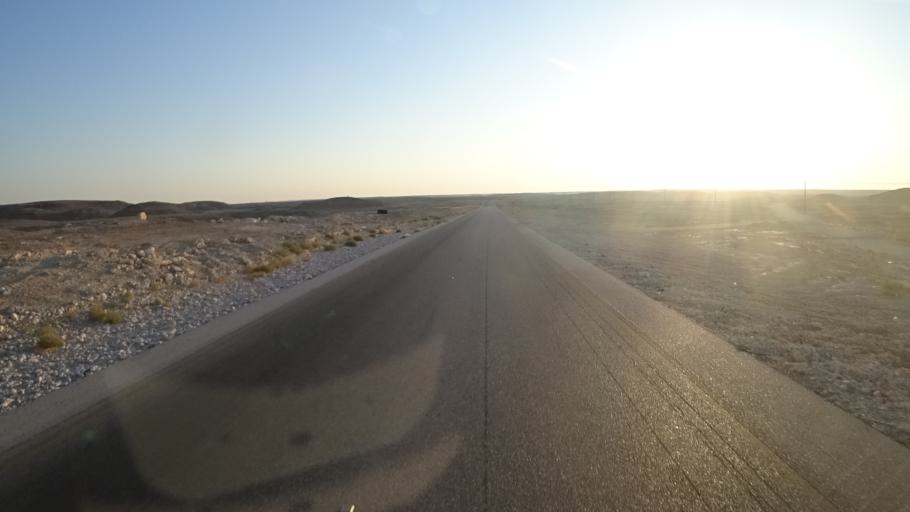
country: OM
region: Zufar
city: Salalah
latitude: 17.5314
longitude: 53.4024
